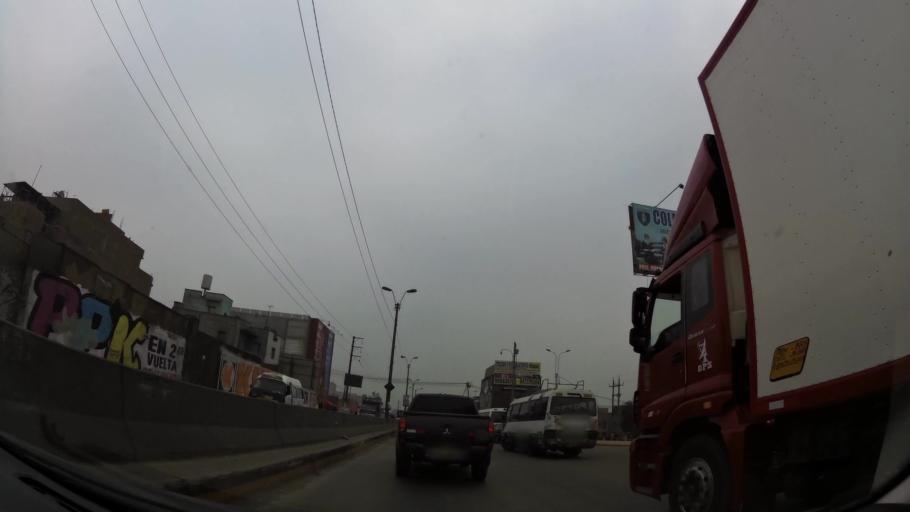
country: PE
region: Lima
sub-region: Lima
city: Santa Maria
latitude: -12.0195
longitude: -76.9002
